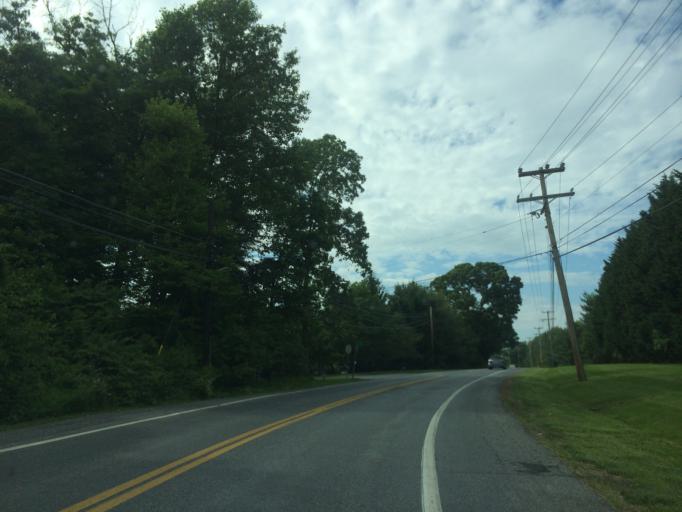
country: US
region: Maryland
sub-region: Howard County
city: Highland
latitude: 39.2220
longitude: -76.9743
